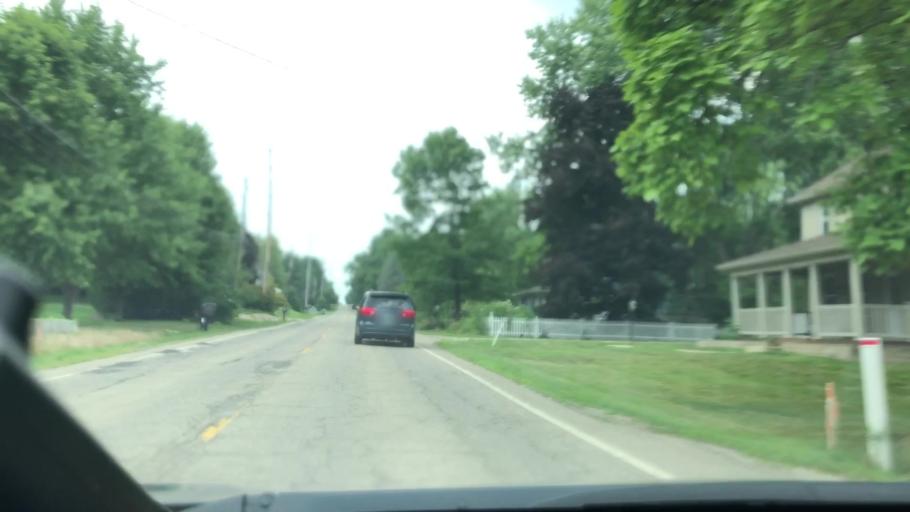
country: US
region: Ohio
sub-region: Summit County
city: New Franklin
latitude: 40.9239
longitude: -81.5356
